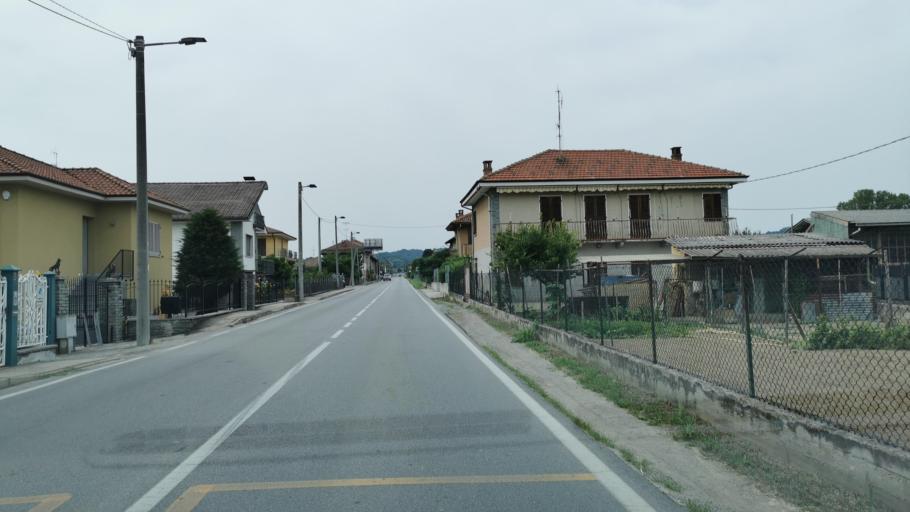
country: IT
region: Piedmont
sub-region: Provincia di Cuneo
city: Cinzano
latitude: 44.6877
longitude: 7.8953
